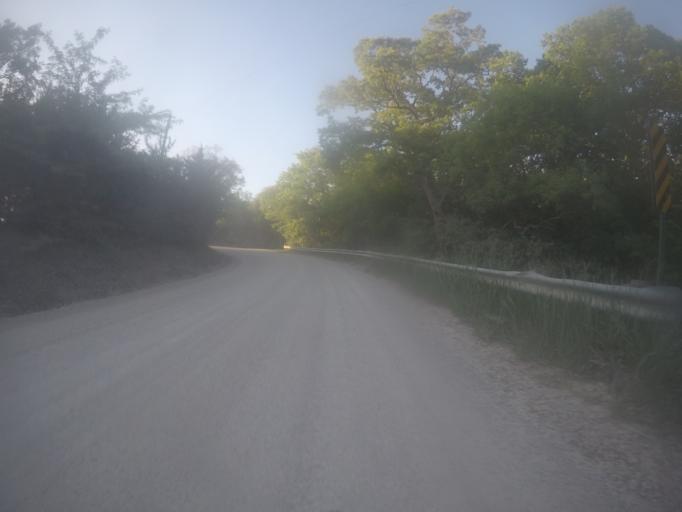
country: US
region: Kansas
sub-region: Riley County
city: Manhattan
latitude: 39.2325
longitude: -96.5480
